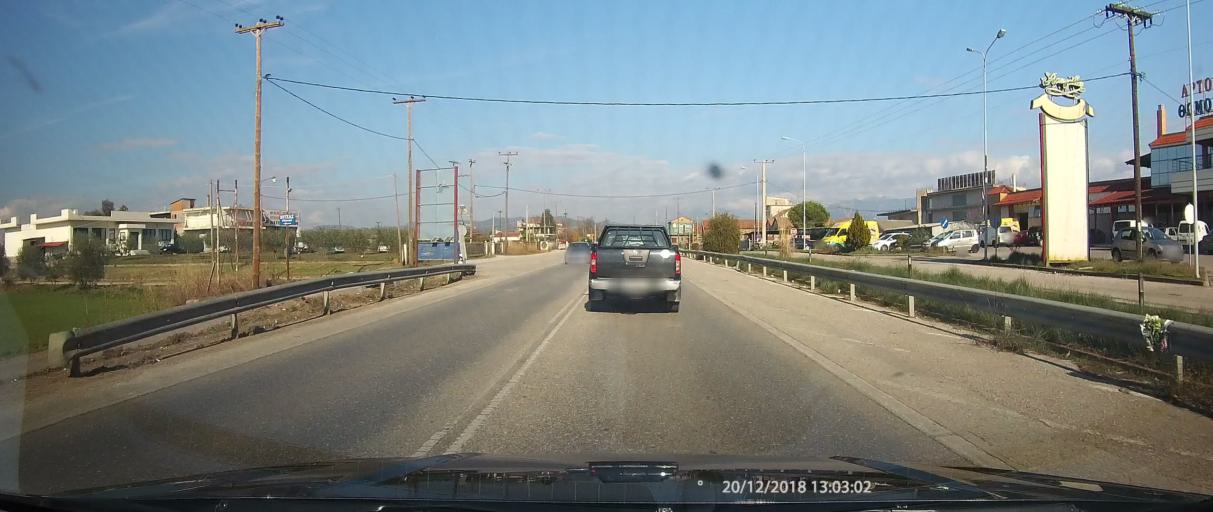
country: GR
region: West Greece
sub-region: Nomos Aitolias kai Akarnanias
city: Panaitolion
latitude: 38.5771
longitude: 21.4251
